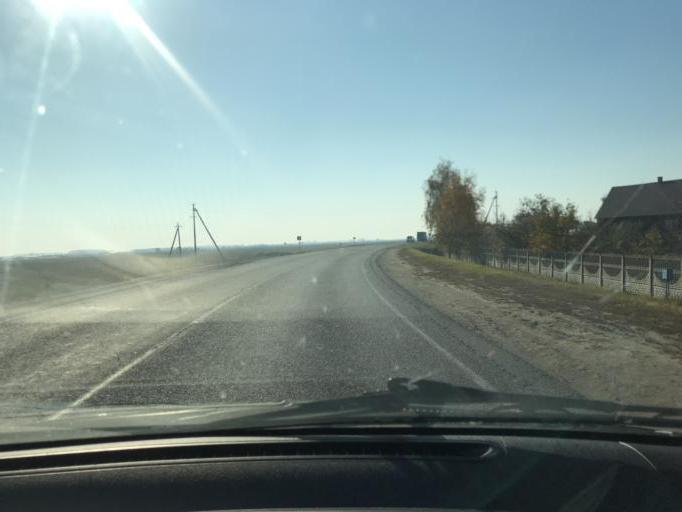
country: BY
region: Brest
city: Davyd-Haradok
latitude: 52.0671
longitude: 27.3358
